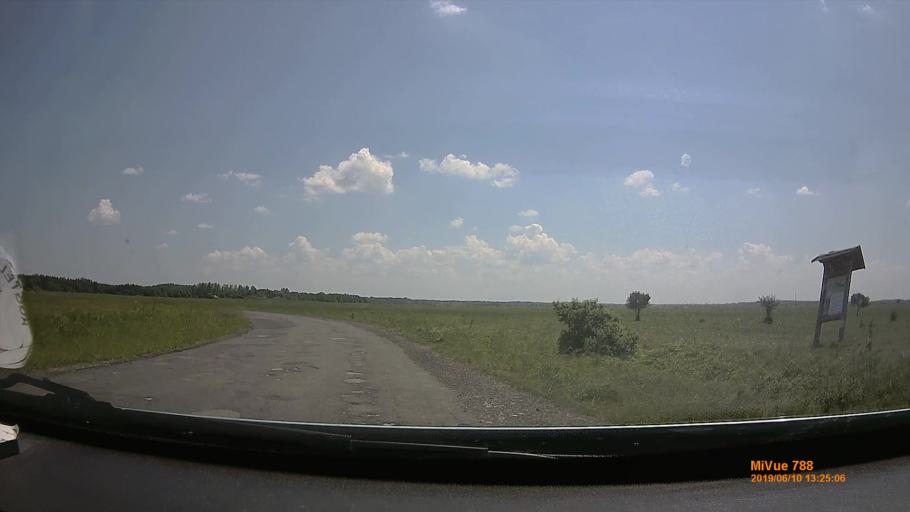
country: HU
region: Borsod-Abauj-Zemplen
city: Tiszaluc
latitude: 48.0171
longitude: 21.1066
